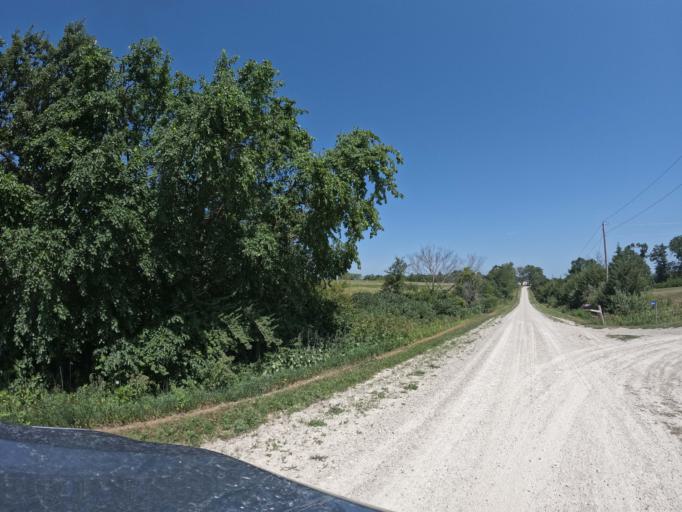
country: US
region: Iowa
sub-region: Henry County
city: Mount Pleasant
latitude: 40.8893
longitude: -91.5745
